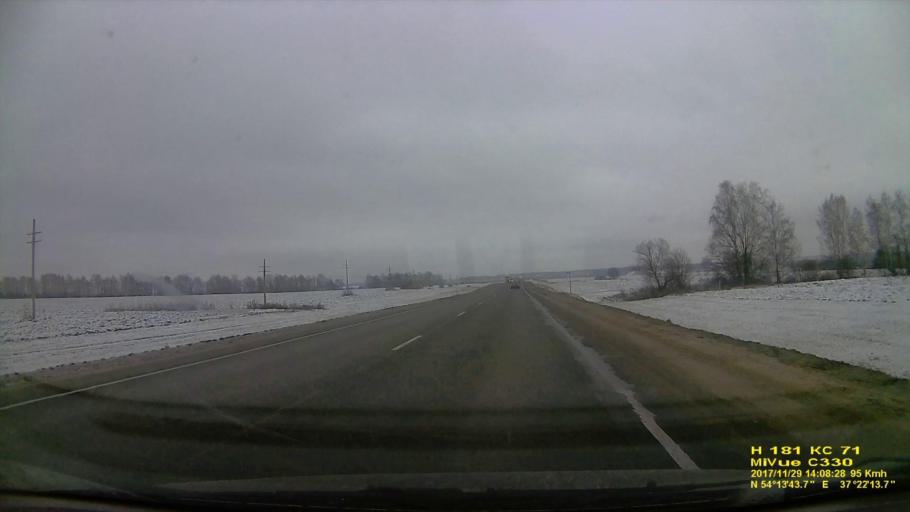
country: RU
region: Tula
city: Leninskiy
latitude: 54.2287
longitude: 37.3708
